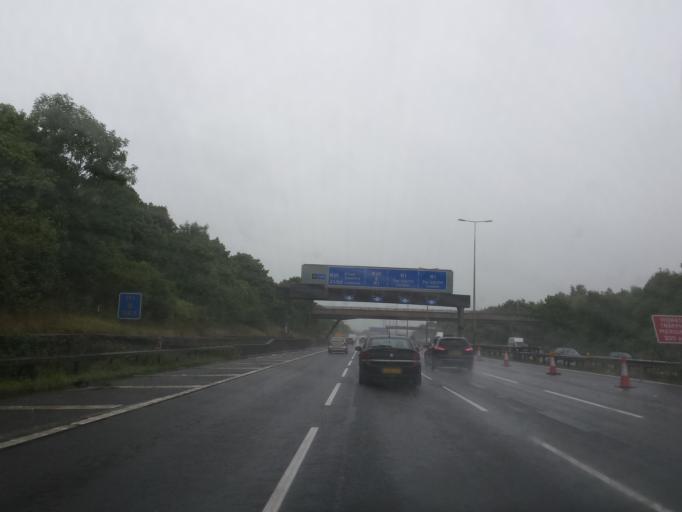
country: GB
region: England
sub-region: Leicestershire
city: Enderby
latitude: 52.6123
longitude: -1.2006
